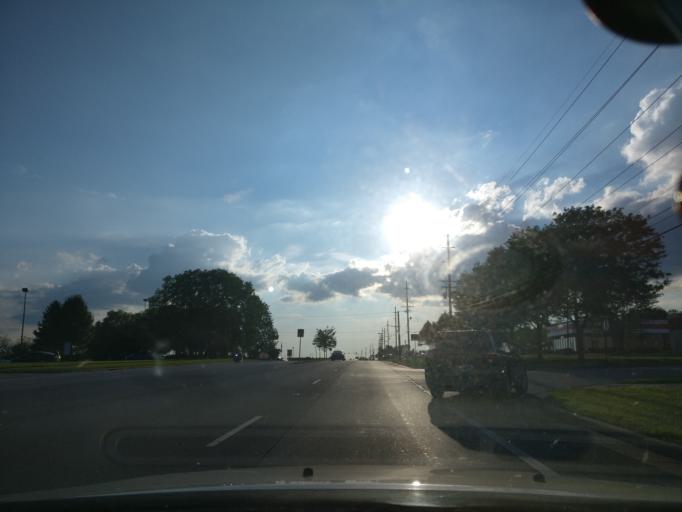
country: US
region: Ohio
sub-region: Warren County
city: Springboro
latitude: 39.5623
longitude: -84.2573
